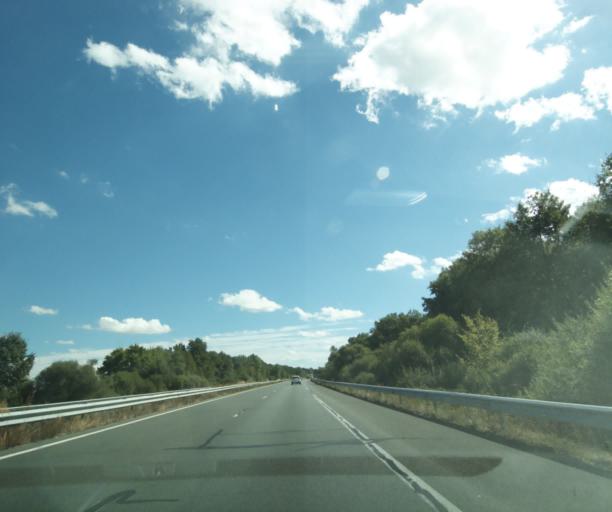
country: FR
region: Aquitaine
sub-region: Departement du Lot-et-Garonne
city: Fourques-sur-Garonne
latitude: 44.4203
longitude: 0.1713
